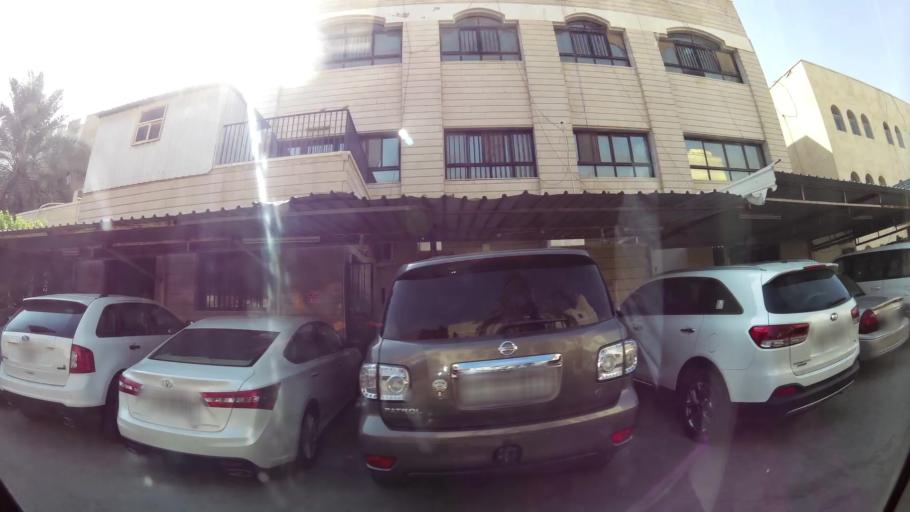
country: KW
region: Muhafazat Hawalli
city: Salwa
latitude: 29.2880
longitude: 48.0791
